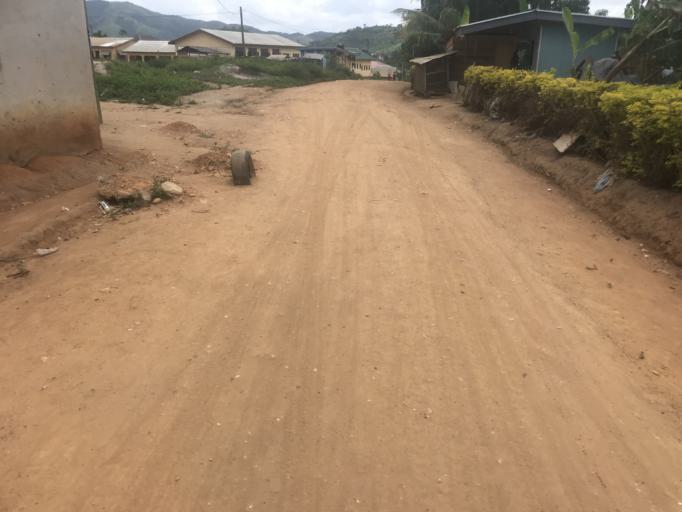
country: GH
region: Ashanti
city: Obuasi
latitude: 6.2021
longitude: -1.5982
